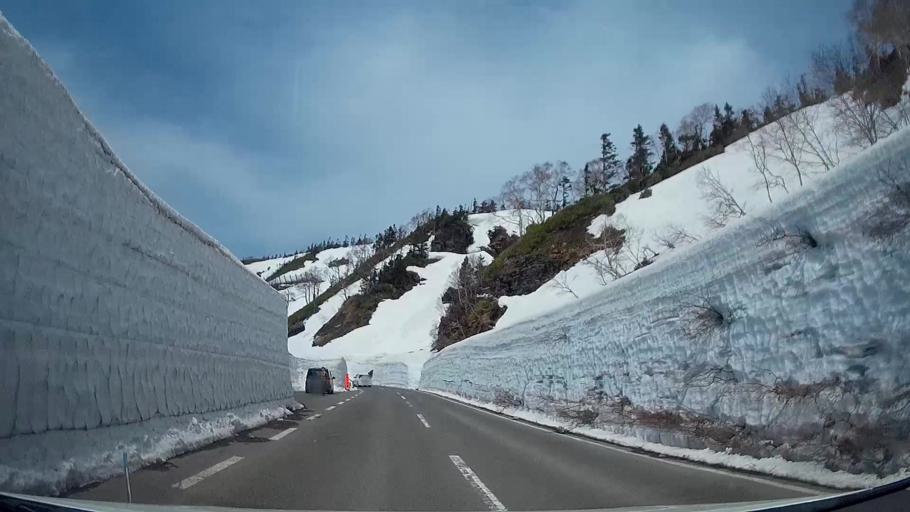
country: JP
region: Akita
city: Hanawa
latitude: 39.9520
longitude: 140.8700
